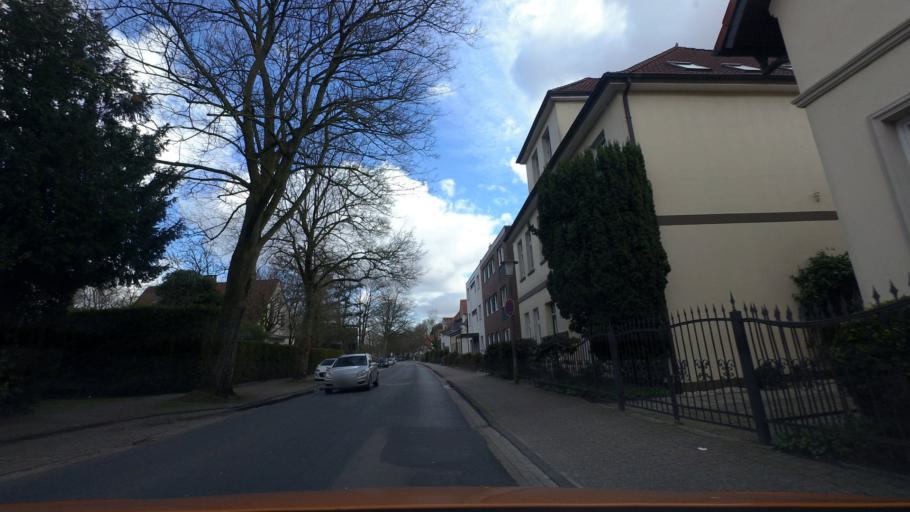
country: DE
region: Lower Saxony
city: Oldenburg
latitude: 53.1407
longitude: 8.1933
